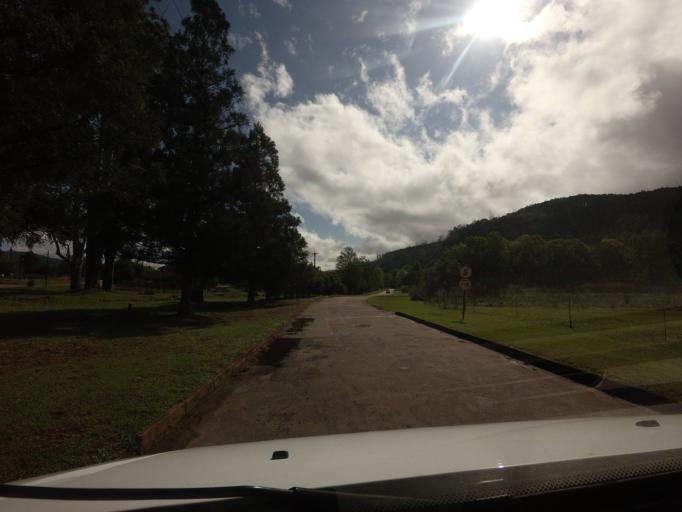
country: ZA
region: Mpumalanga
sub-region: Ehlanzeni District
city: Graksop
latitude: -25.0935
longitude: 30.7715
